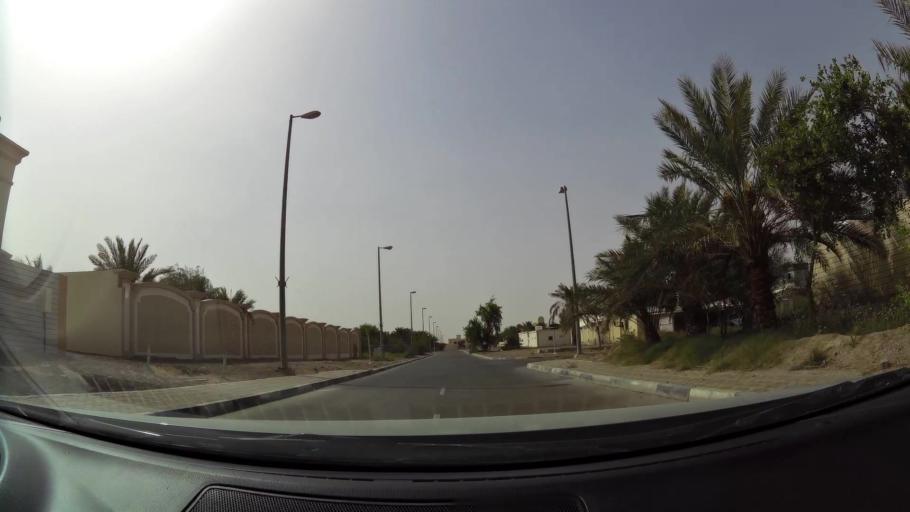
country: AE
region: Abu Dhabi
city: Al Ain
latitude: 24.1893
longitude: 55.6396
